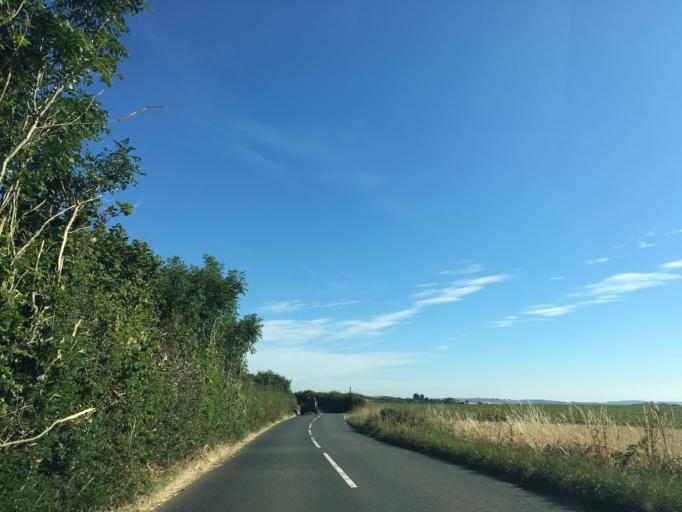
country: GB
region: England
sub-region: Isle of Wight
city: Niton
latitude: 50.6156
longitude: -1.2820
